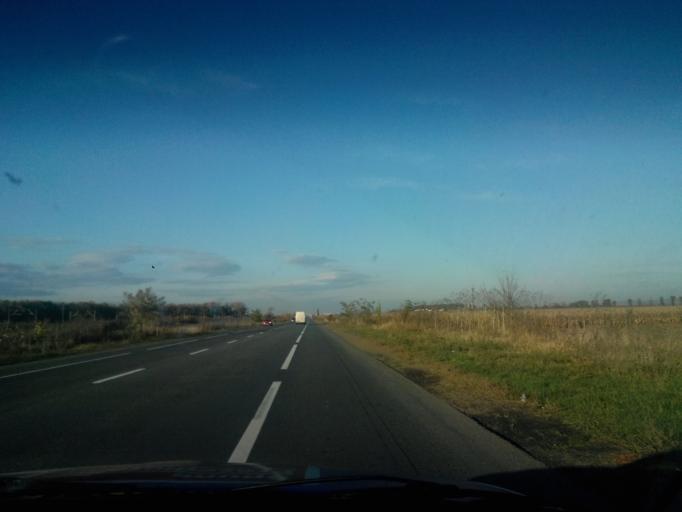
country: RO
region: Neamt
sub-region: Municipiul Roman
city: Roman
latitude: 46.8653
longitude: 26.8922
